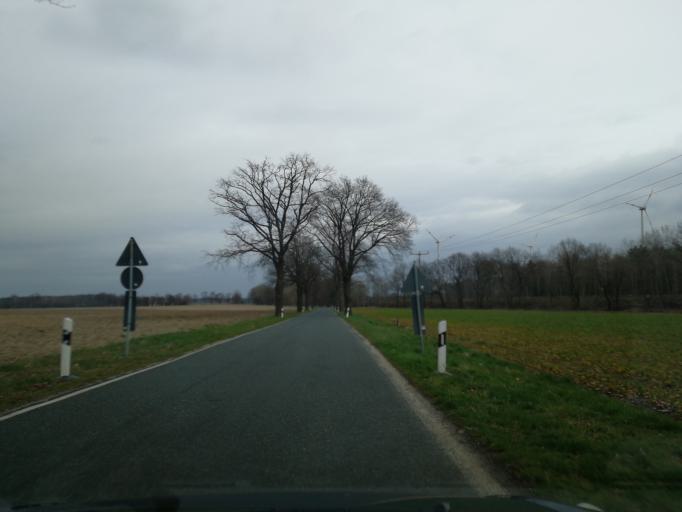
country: DE
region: Brandenburg
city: Calau
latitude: 51.7440
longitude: 13.9929
